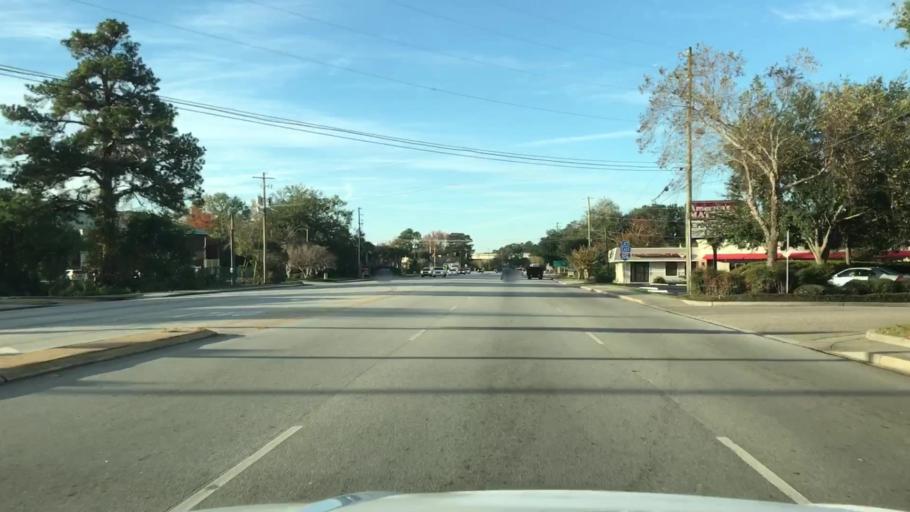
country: US
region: South Carolina
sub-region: Charleston County
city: Shell Point
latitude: 32.7945
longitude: -80.0282
